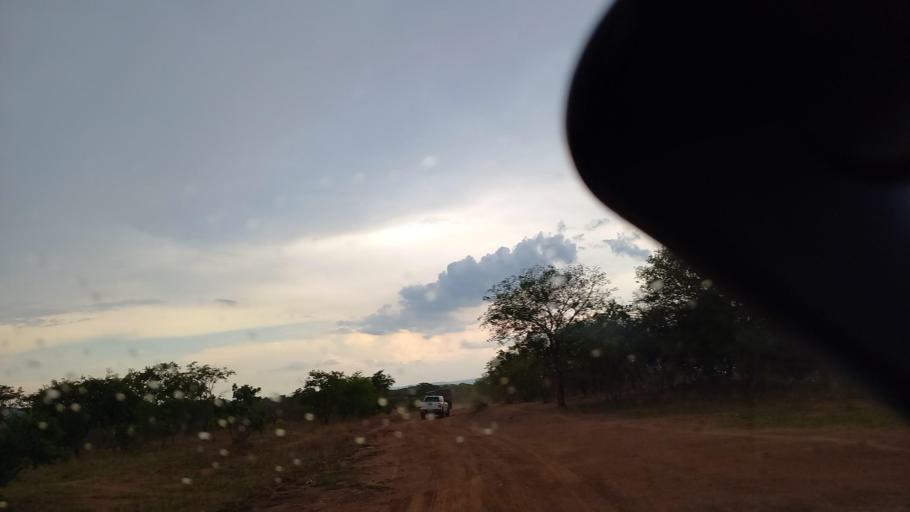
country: ZM
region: Lusaka
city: Kafue
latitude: -15.9802
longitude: 28.2578
